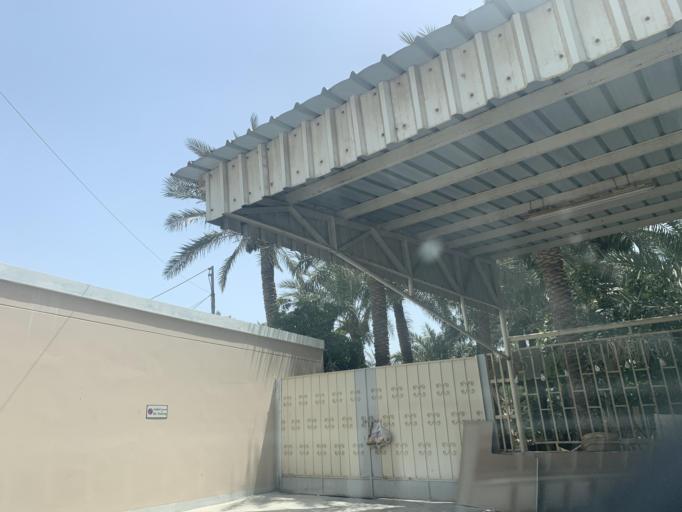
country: BH
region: Manama
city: Jidd Hafs
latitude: 26.2030
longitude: 50.5369
